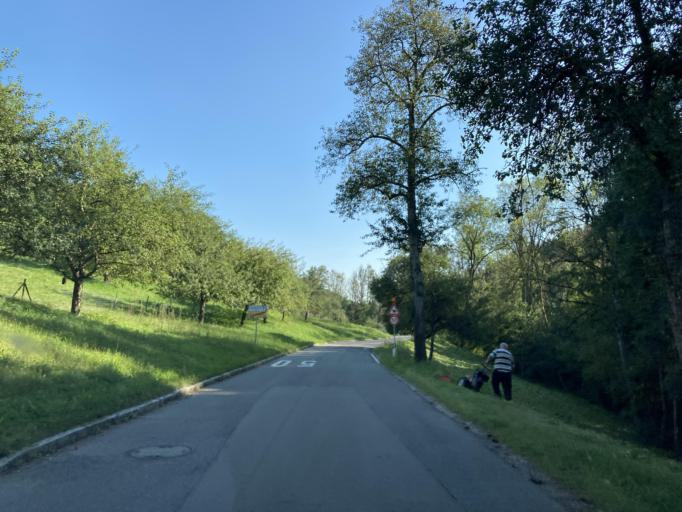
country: DE
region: Baden-Wuerttemberg
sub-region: Freiburg Region
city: Blumberg
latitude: 47.8594
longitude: 8.5035
